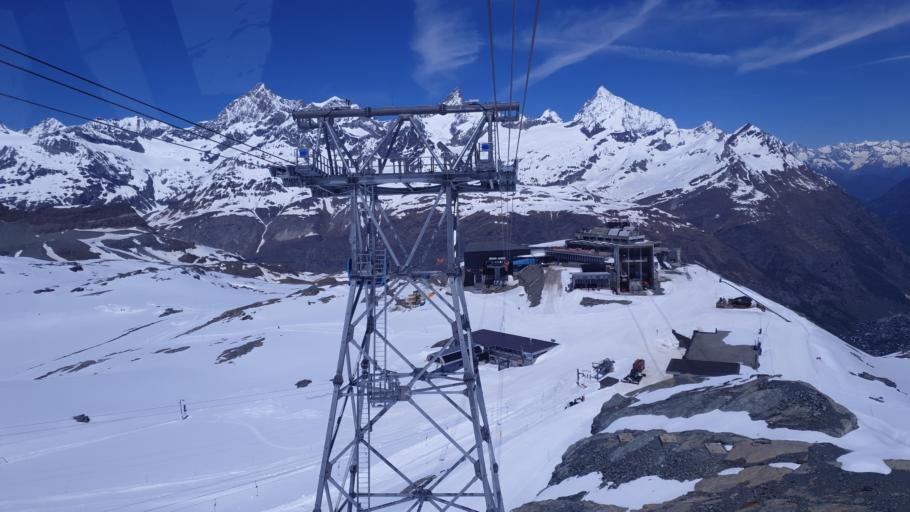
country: CH
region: Valais
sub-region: Visp District
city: Zermatt
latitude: 45.9678
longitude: 7.7224
